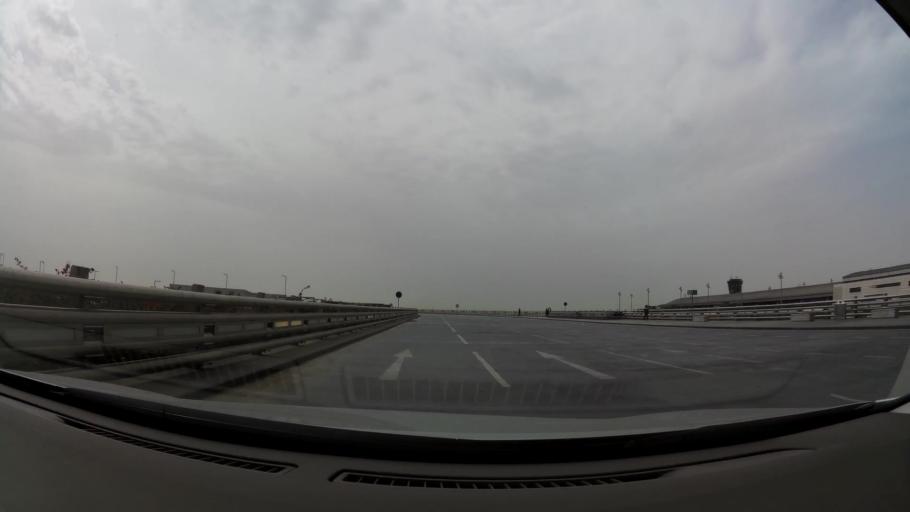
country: QA
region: Al Wakrah
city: Al Wakrah
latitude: 25.2592
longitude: 51.6130
